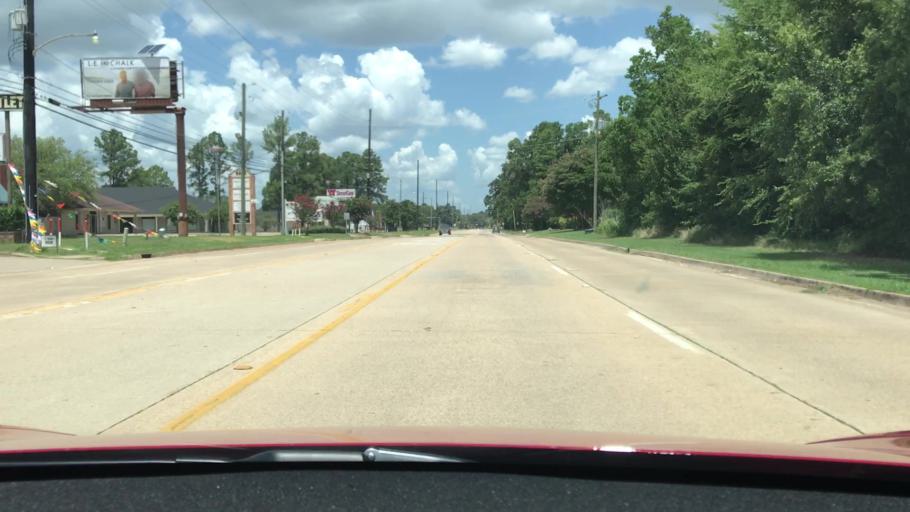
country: US
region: Louisiana
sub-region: Bossier Parish
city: Bossier City
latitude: 32.4238
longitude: -93.7385
